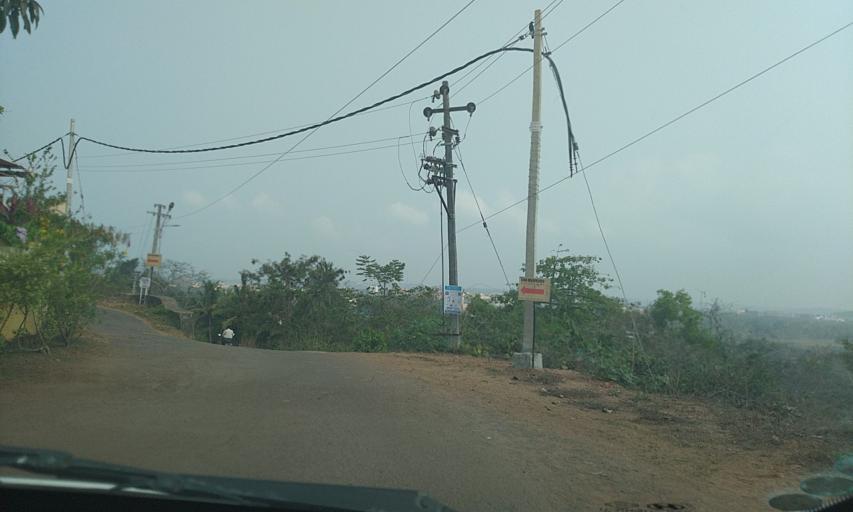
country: IN
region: Goa
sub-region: North Goa
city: Taleigao
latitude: 15.4627
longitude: 73.8169
